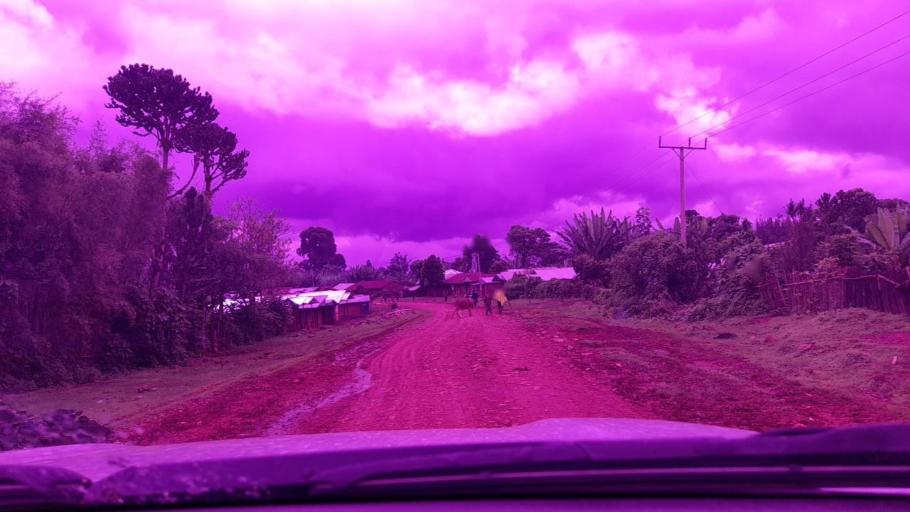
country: ET
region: Southern Nations, Nationalities, and People's Region
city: Tippi
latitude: 7.5791
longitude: 35.6326
